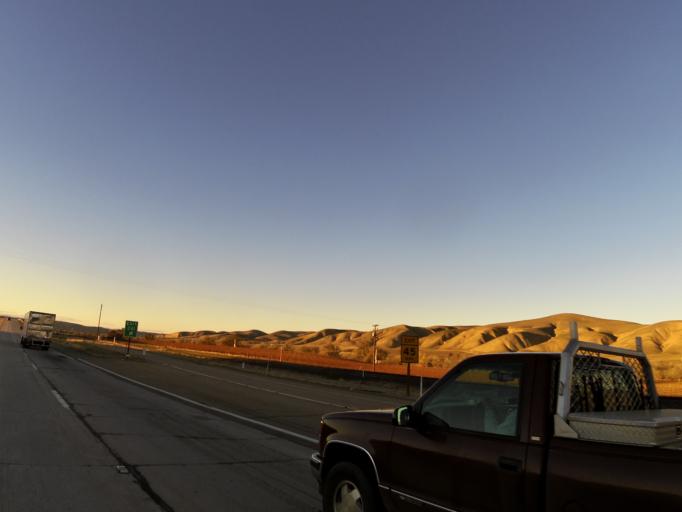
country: US
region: California
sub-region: San Luis Obispo County
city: San Miguel
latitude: 35.7725
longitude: -120.7080
